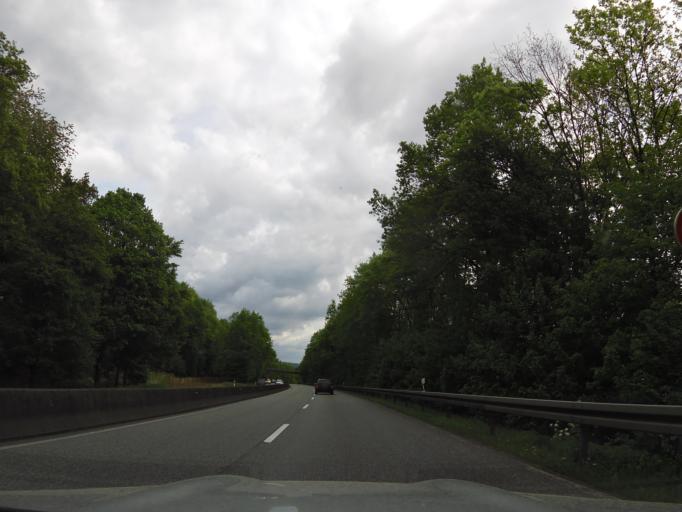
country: DE
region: Hesse
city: Weilburg
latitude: 50.5036
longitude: 8.2401
